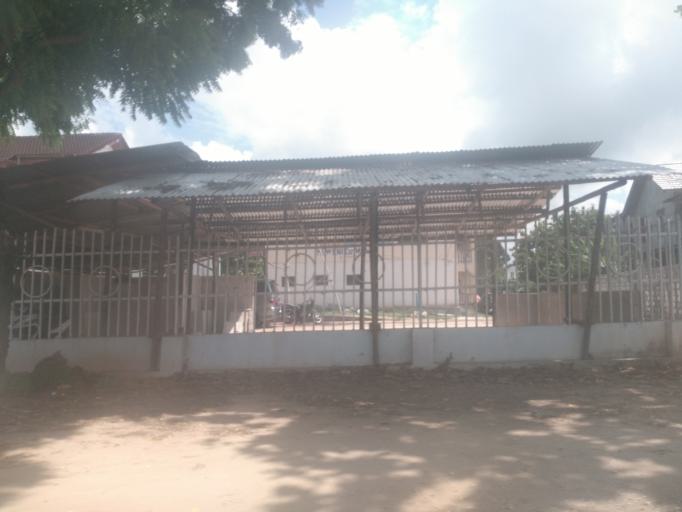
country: TZ
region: Zanzibar Urban/West
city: Zanzibar
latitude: -6.2151
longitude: 39.2118
